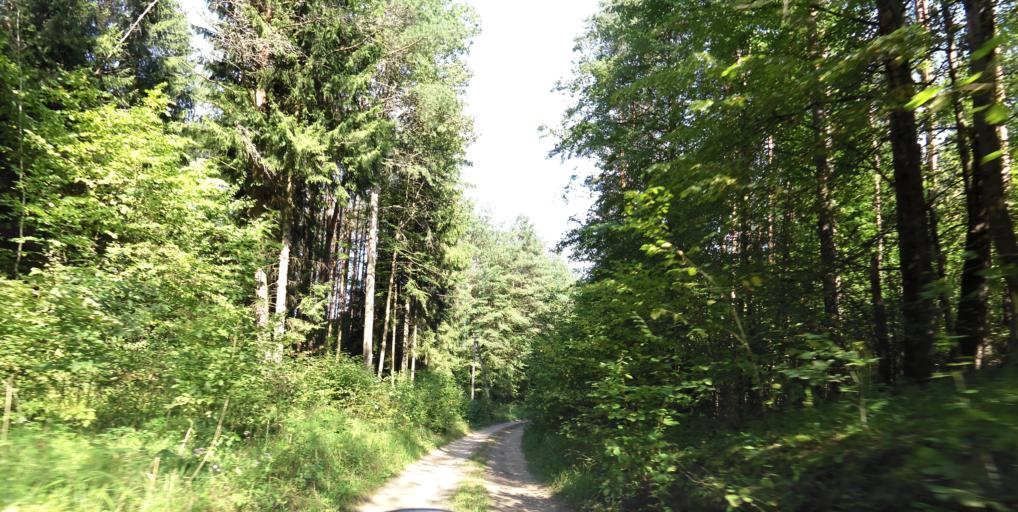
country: LT
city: Grigiskes
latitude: 54.7462
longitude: 25.0229
